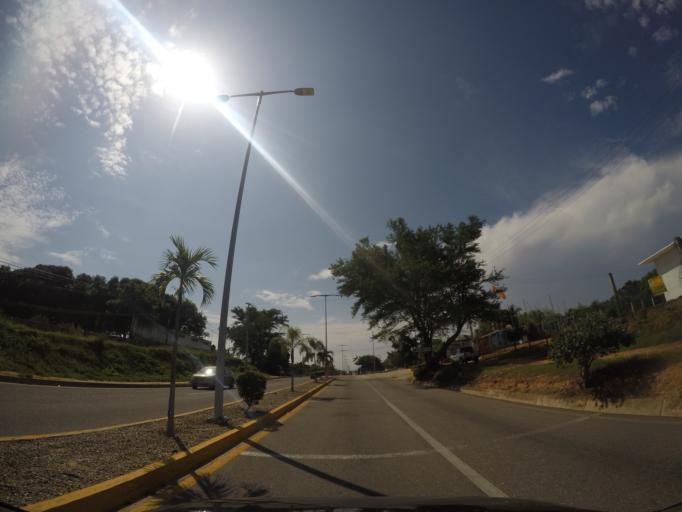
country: MX
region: Oaxaca
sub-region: Santa Maria Colotepec
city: Brisas de Zicatela
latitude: 15.8442
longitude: -97.0451
